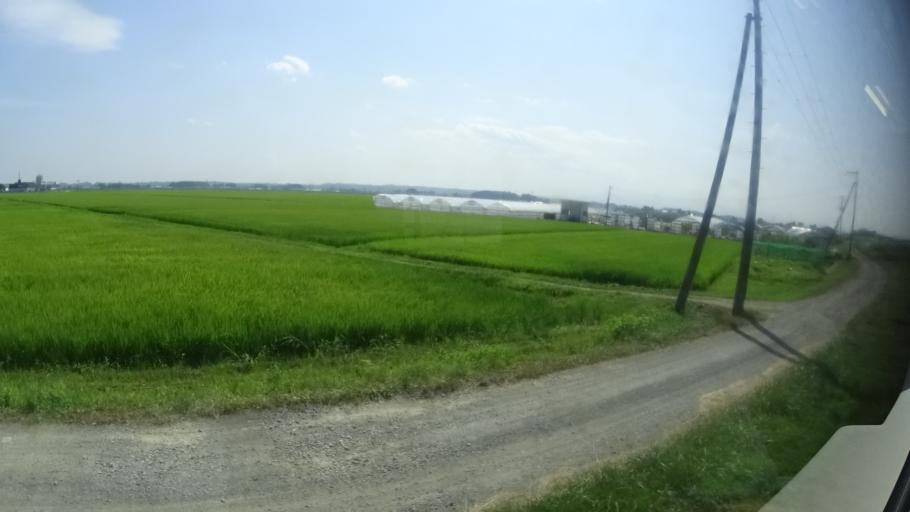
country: JP
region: Miyagi
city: Wakuya
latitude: 38.5502
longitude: 141.0965
